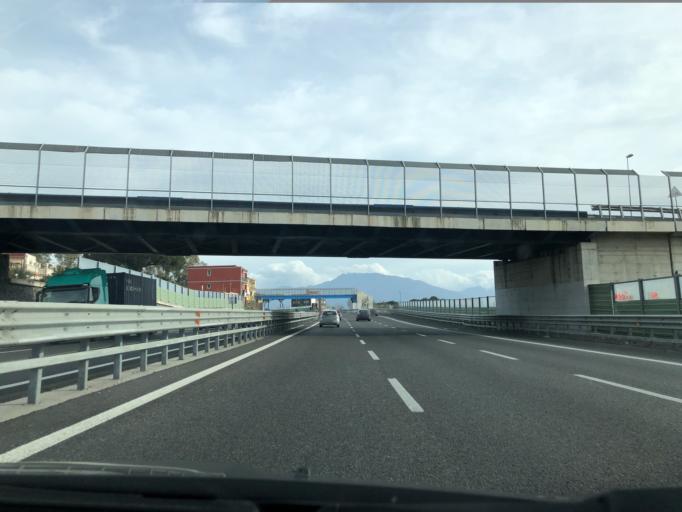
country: IT
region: Campania
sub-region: Provincia di Napoli
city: Torre del Greco
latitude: 40.7820
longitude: 14.3900
